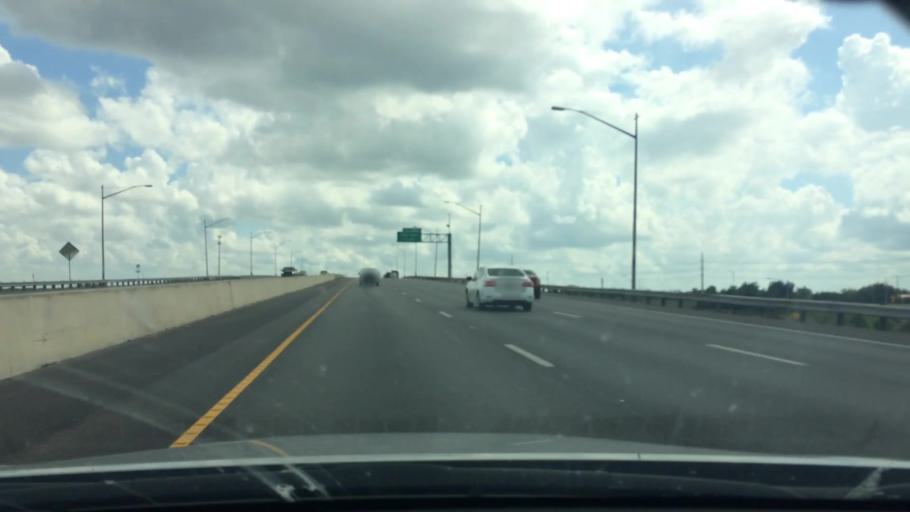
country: US
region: Texas
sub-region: Bexar County
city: San Antonio
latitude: 29.3976
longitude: -98.4794
